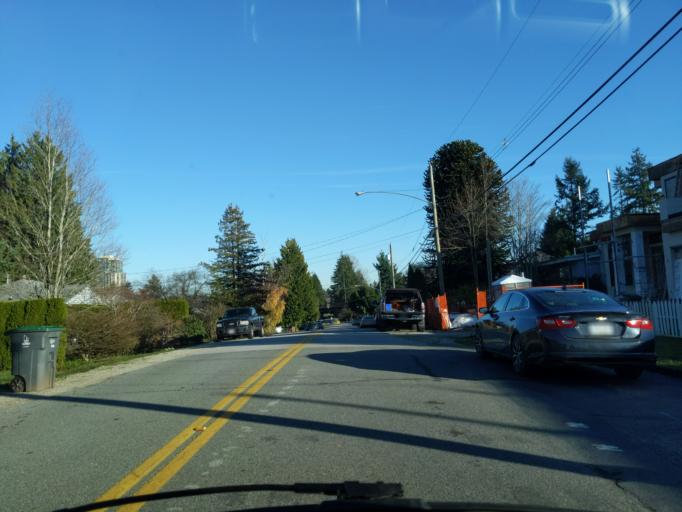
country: CA
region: British Columbia
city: New Westminster
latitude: 49.1962
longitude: -122.8593
